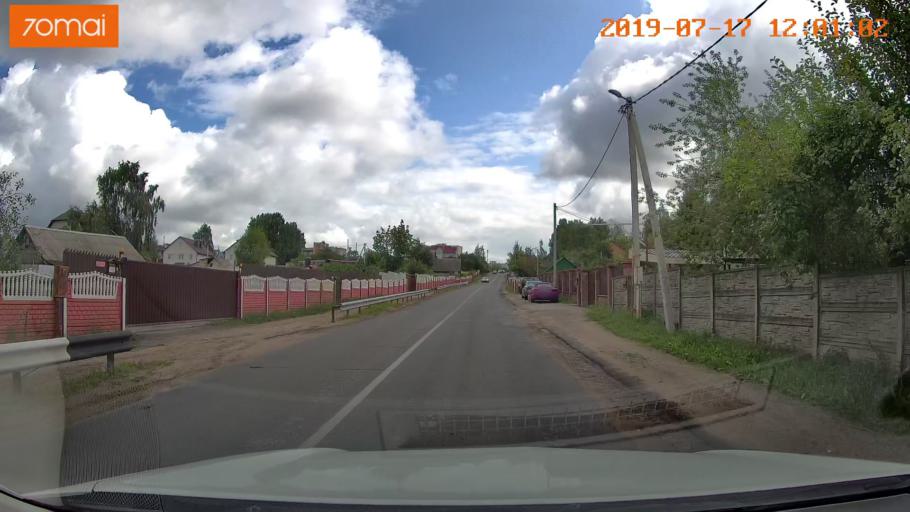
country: BY
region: Minsk
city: Borovlyany
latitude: 54.0045
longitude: 27.6719
